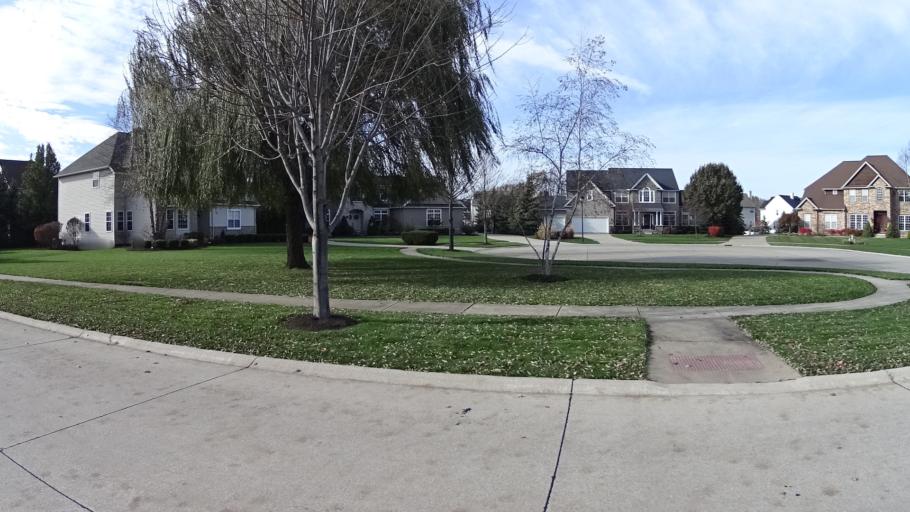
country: US
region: Ohio
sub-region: Lorain County
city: Avon Lake
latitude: 41.4941
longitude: -82.0320
